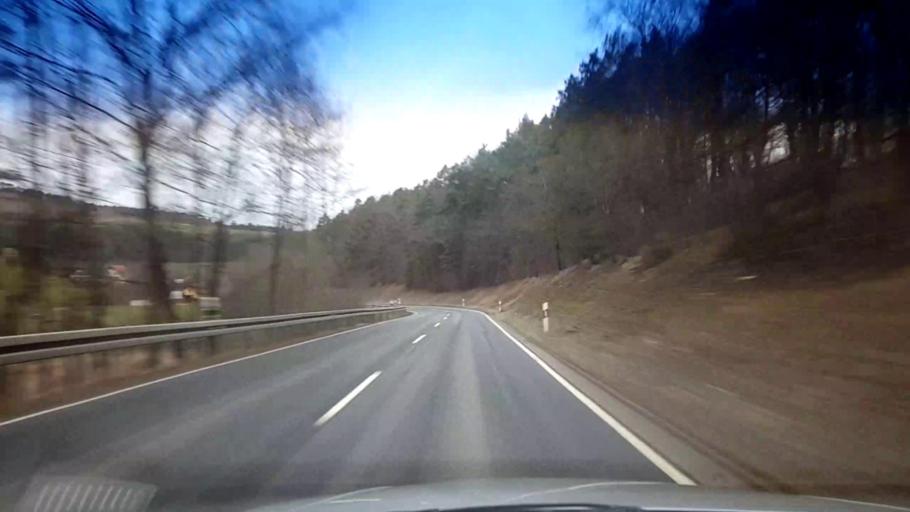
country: DE
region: Bavaria
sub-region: Upper Franconia
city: Wattendorf
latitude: 50.0542
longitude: 11.0794
